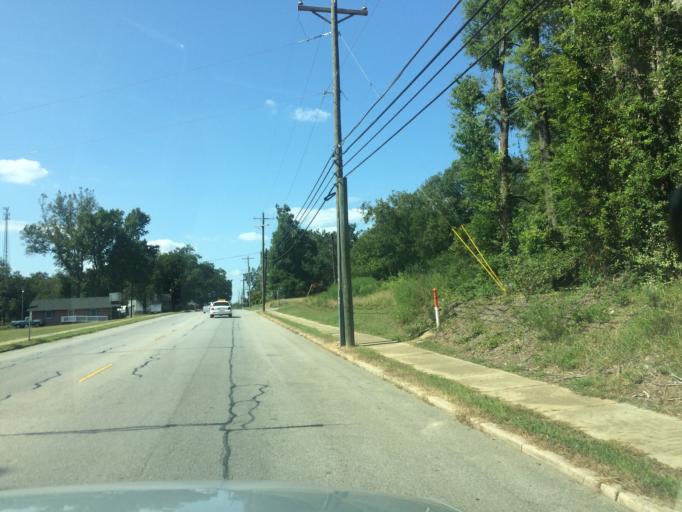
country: US
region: South Carolina
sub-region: Lexington County
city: Batesburg
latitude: 33.9006
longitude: -81.5423
